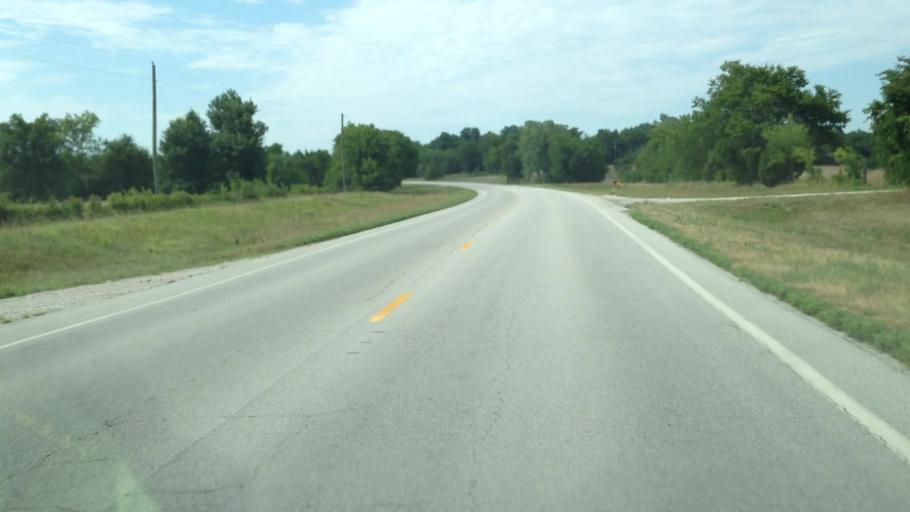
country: US
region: Kansas
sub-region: Labette County
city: Oswego
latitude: 37.1448
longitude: -95.1036
